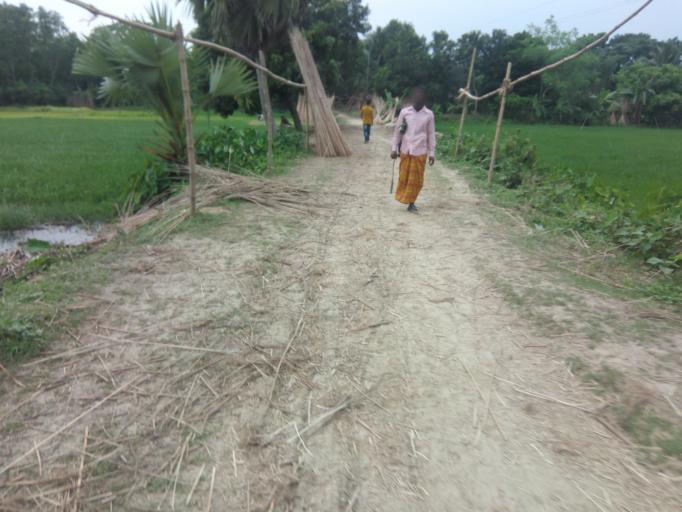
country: BD
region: Khulna
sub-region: Magura
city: Magura
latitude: 23.5072
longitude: 89.6066
